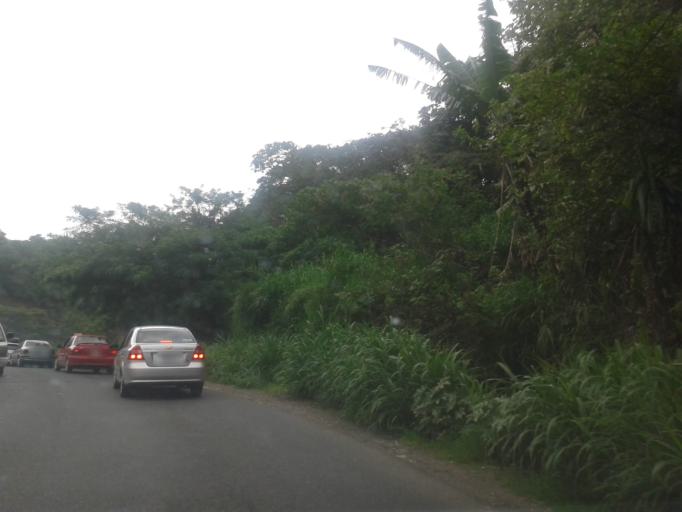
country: CR
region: San Jose
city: San Juan
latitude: 9.9666
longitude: -84.0851
